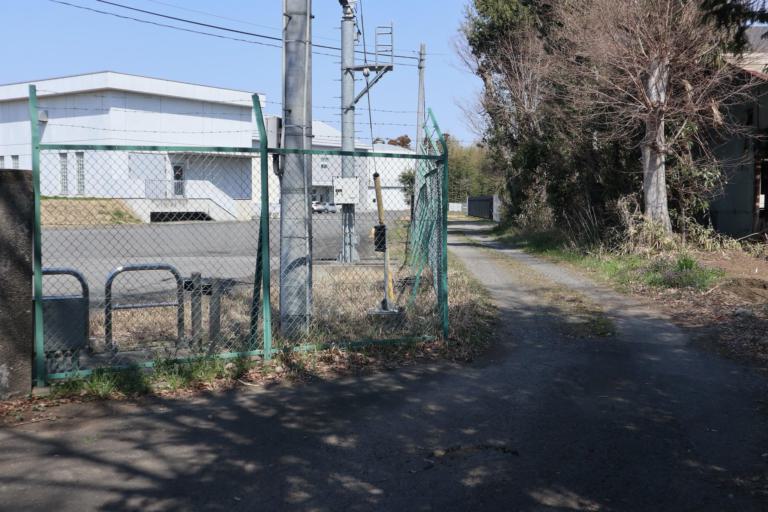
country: JP
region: Ibaraki
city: Koga
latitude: 36.2207
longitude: 139.7113
